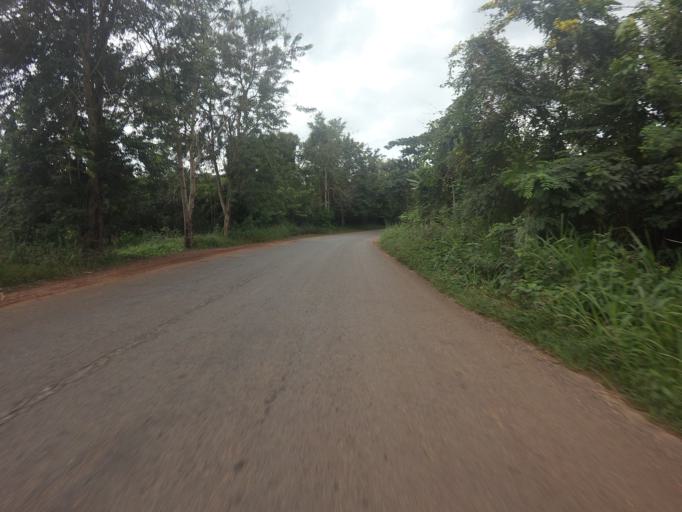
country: GH
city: Akropong
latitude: 5.9587
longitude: -0.1259
